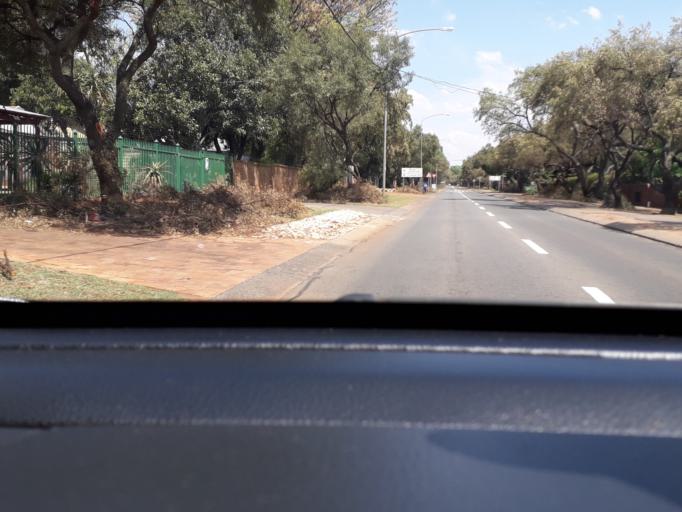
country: ZA
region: Gauteng
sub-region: City of Tshwane Metropolitan Municipality
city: Centurion
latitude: -25.8217
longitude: 28.2070
